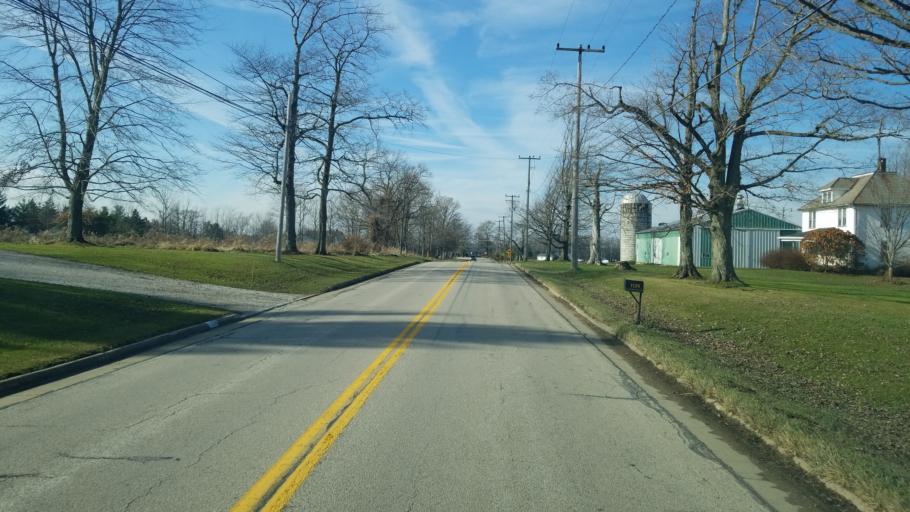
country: US
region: Ohio
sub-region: Ashtabula County
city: Jefferson
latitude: 41.7385
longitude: -80.7912
